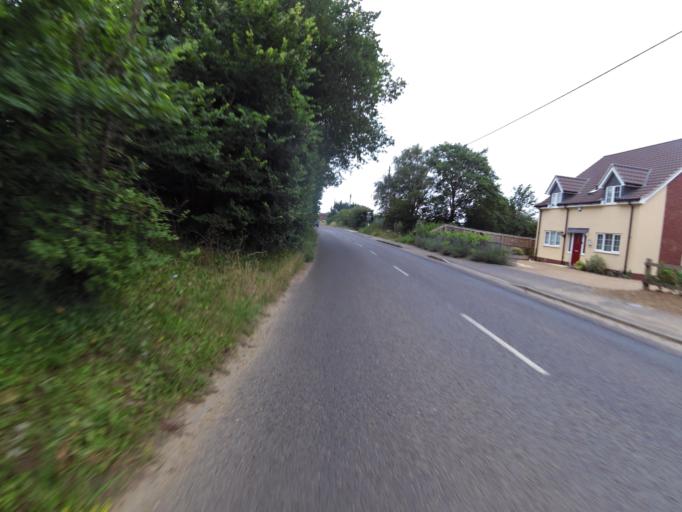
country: GB
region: England
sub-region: Suffolk
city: Bramford
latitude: 52.0814
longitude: 1.0923
